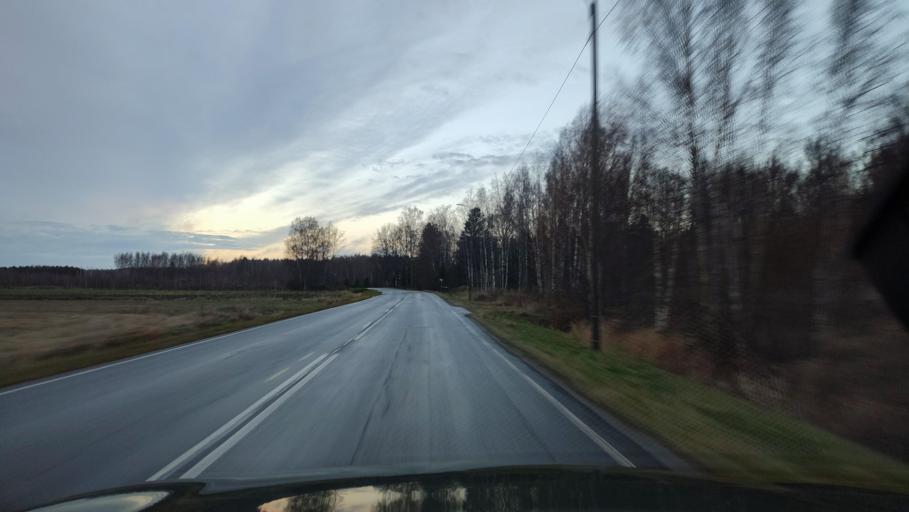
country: FI
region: Ostrobothnia
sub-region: Vaasa
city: Ristinummi
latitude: 63.0472
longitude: 21.7420
